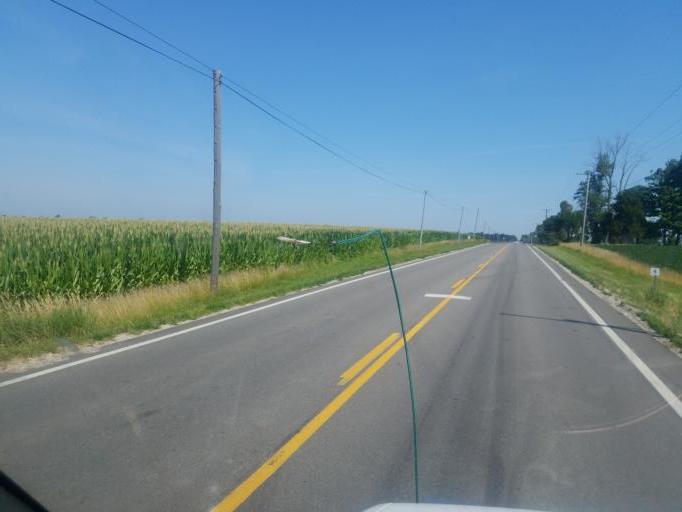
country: US
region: Ohio
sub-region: Union County
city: Marysville
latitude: 40.2915
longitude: -83.3793
